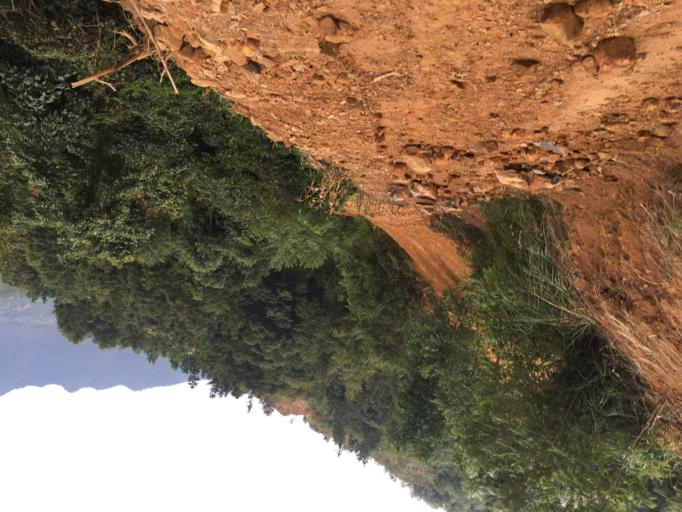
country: CN
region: Guangxi Zhuangzu Zizhiqu
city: Tongle
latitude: 25.3020
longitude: 106.1465
